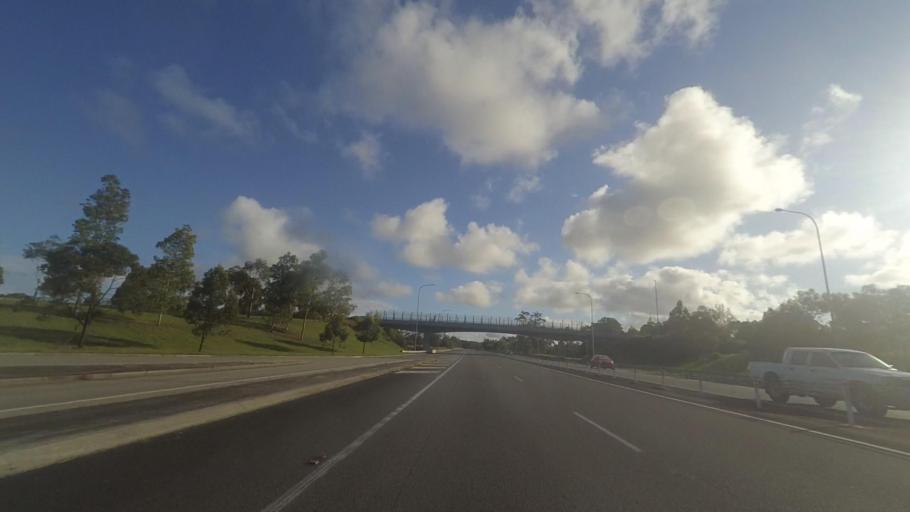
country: AU
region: New South Wales
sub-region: Great Lakes
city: Nabiac
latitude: -32.1004
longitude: 152.3755
